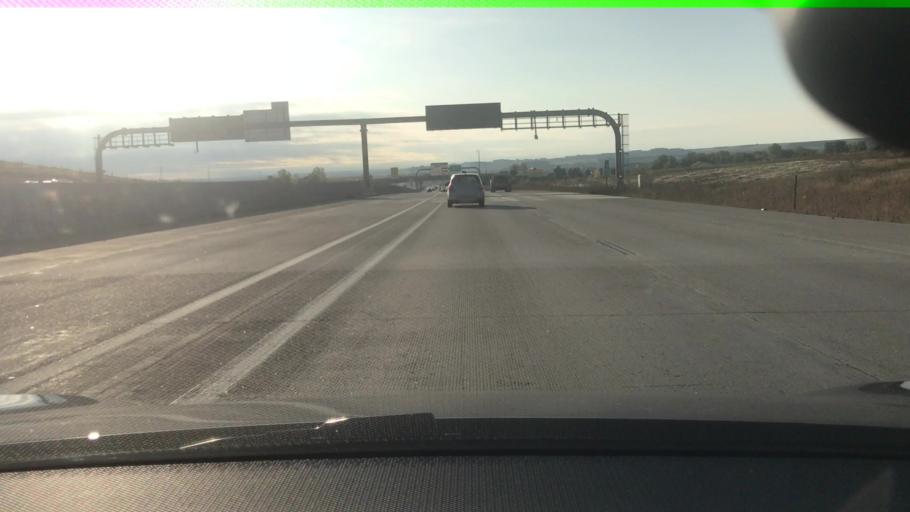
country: US
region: Colorado
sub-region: Boulder County
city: Superior
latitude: 39.9493
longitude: -105.1518
